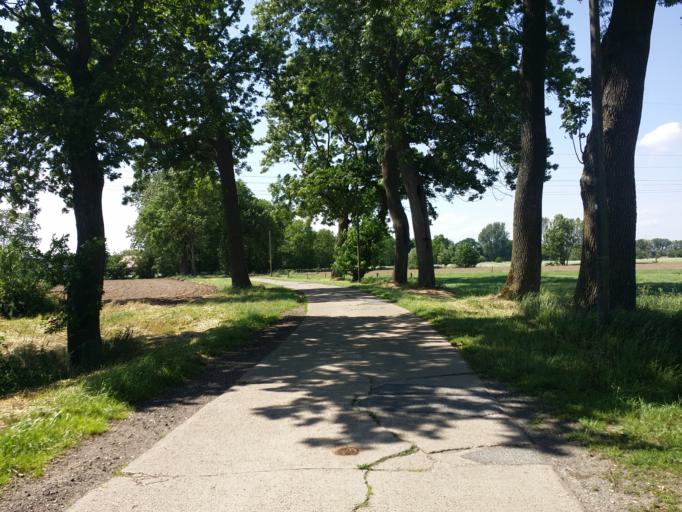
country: DE
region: Lower Saxony
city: Neuenkirchen
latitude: 53.1620
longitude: 8.5181
